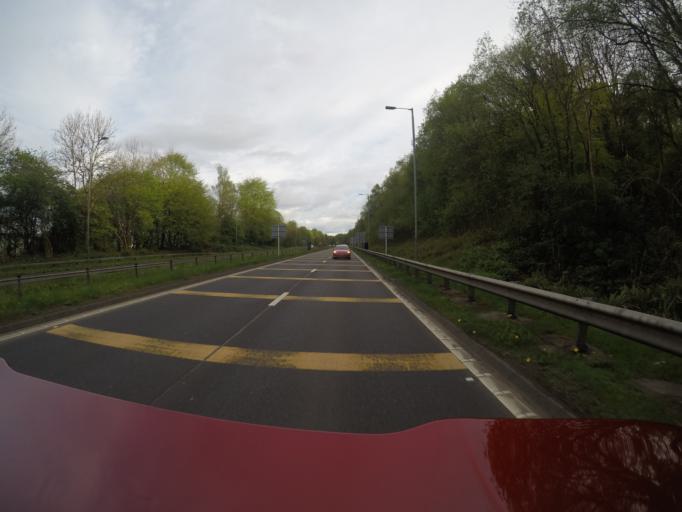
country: GB
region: Scotland
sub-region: West Dunbartonshire
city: Alexandria
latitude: 55.9962
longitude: -4.5961
